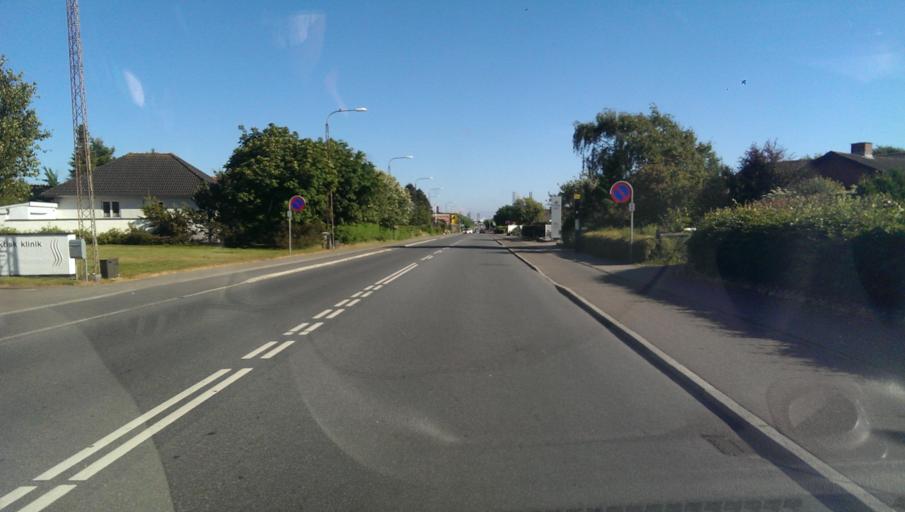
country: DK
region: South Denmark
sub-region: Esbjerg Kommune
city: Esbjerg
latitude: 55.4969
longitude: 8.4085
